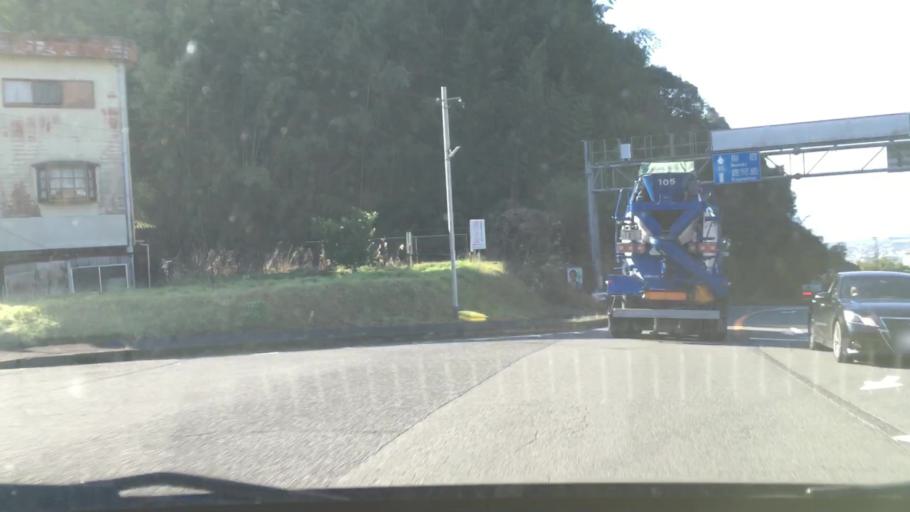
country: JP
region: Kagoshima
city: Kajiki
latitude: 31.7535
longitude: 130.6782
